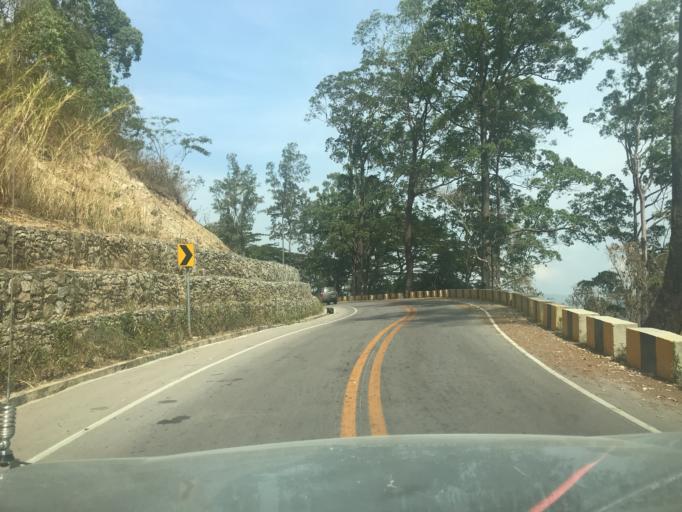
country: TL
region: Aileu
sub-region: Aileu Villa
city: Aileu
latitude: -8.6737
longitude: 125.5529
